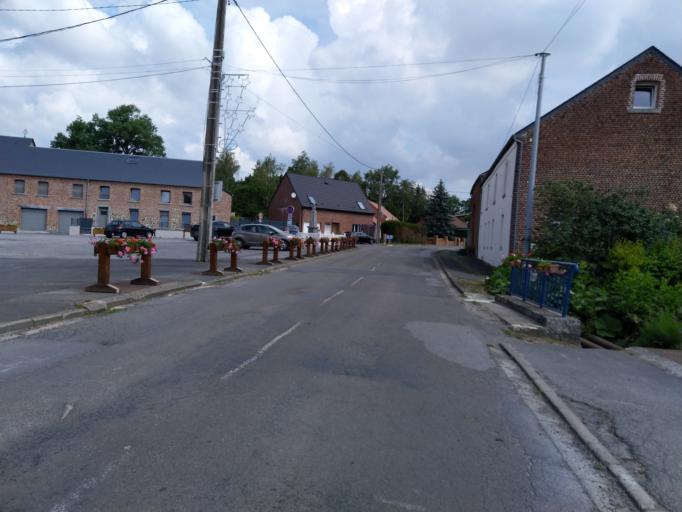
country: FR
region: Nord-Pas-de-Calais
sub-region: Departement du Nord
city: Boussois
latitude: 50.3223
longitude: 4.0058
